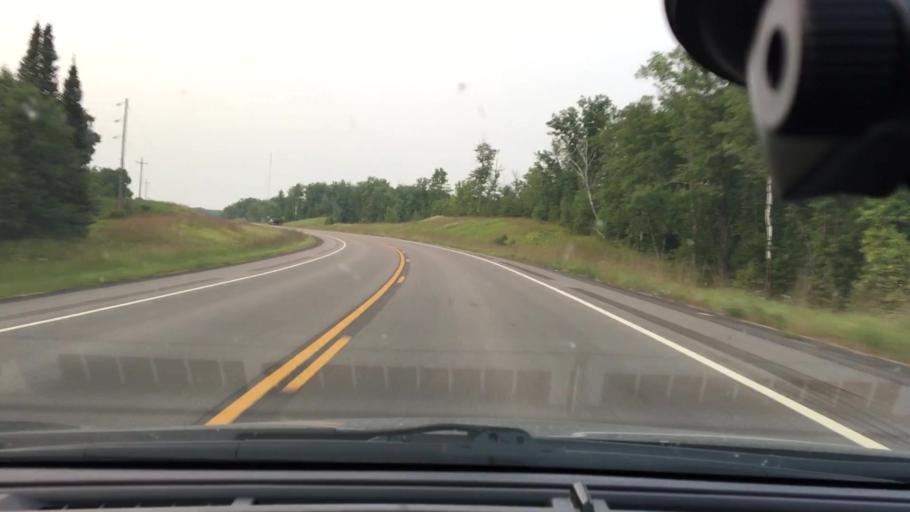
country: US
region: Minnesota
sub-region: Crow Wing County
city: Crosby
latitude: 46.5528
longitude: -93.9531
